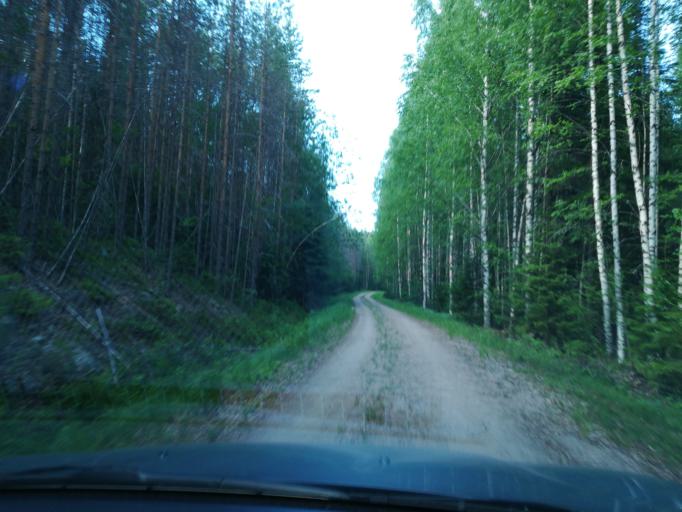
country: FI
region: South Karelia
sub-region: Imatra
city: Ruokolahti
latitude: 61.5459
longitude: 28.8099
